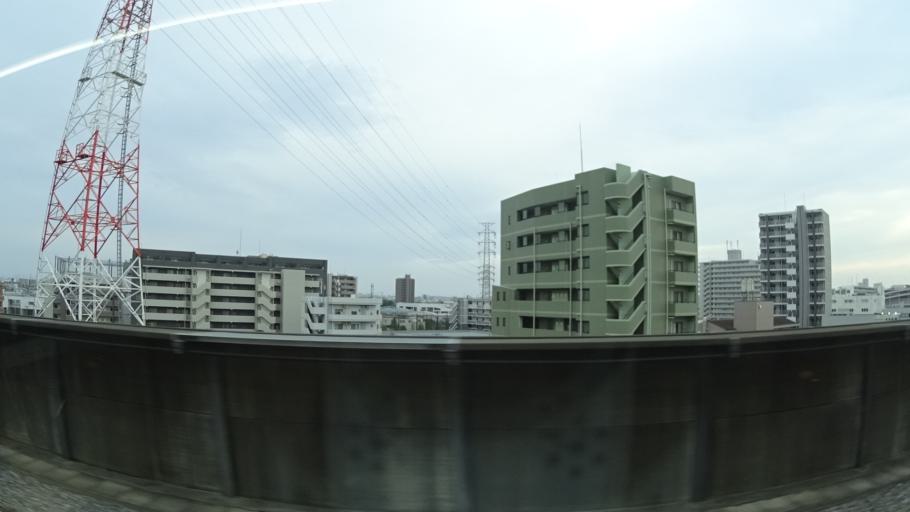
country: JP
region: Saitama
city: Shimotoda
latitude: 35.8272
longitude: 139.6605
